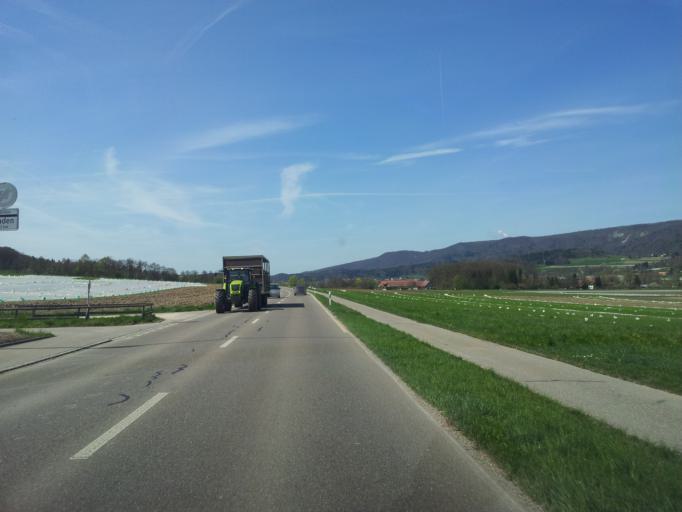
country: CH
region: Zurich
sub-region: Bezirk Dielsdorf
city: Daellikon / Daellikon (Dorf)
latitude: 47.4416
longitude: 8.4311
